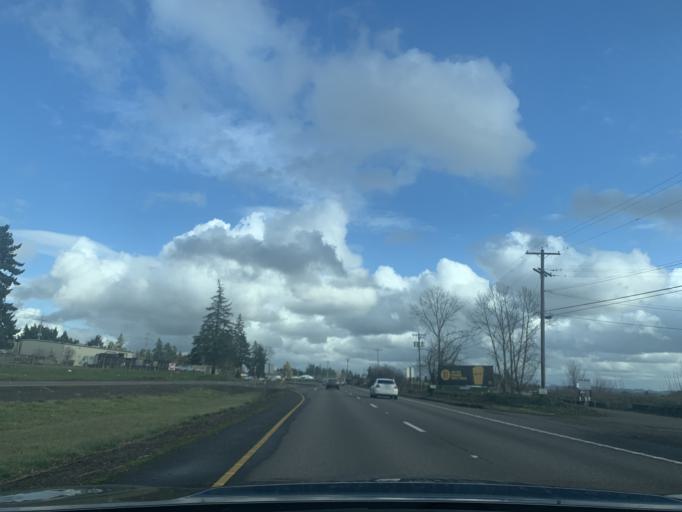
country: US
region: Oregon
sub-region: Washington County
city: King City
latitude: 45.3852
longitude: -122.8144
